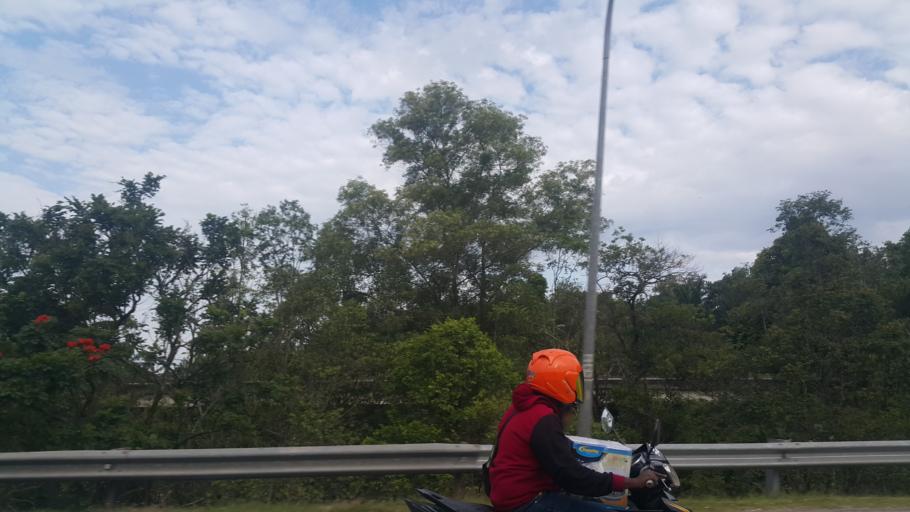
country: MY
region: Johor
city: Pekan Nenas
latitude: 1.4025
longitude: 103.5886
